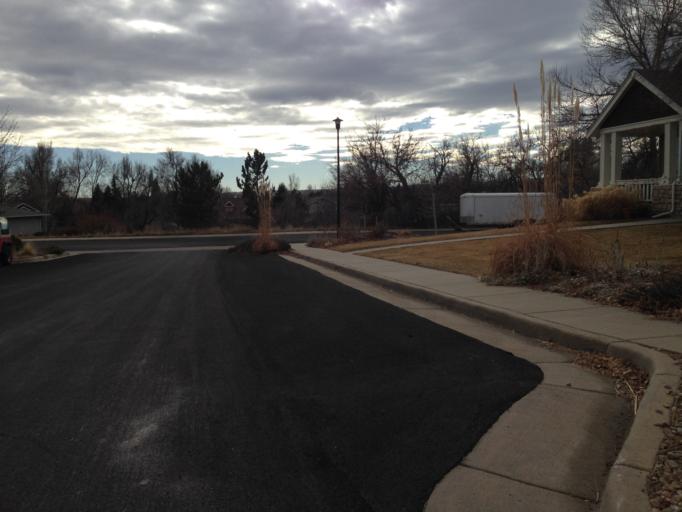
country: US
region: Colorado
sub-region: Boulder County
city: Louisville
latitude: 39.9792
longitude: -105.1403
